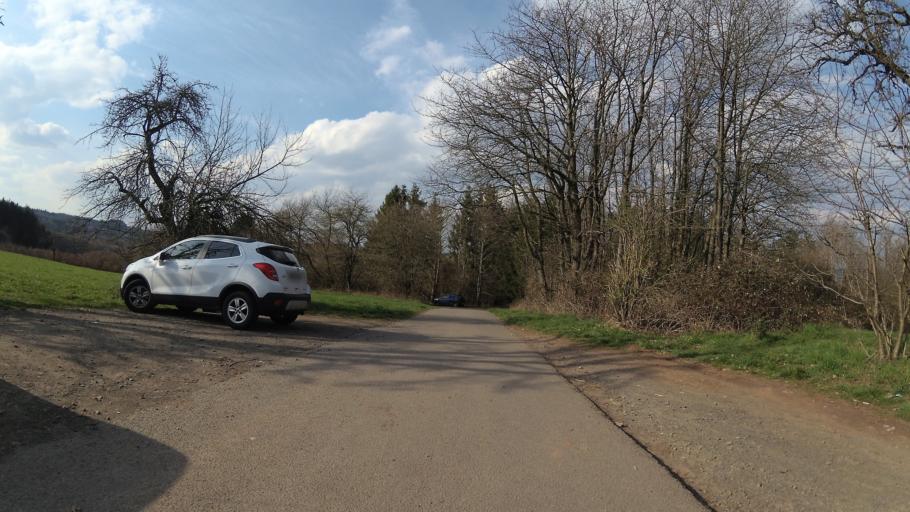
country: DE
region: Saarland
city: Ottweiler
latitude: 49.3999
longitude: 7.1438
